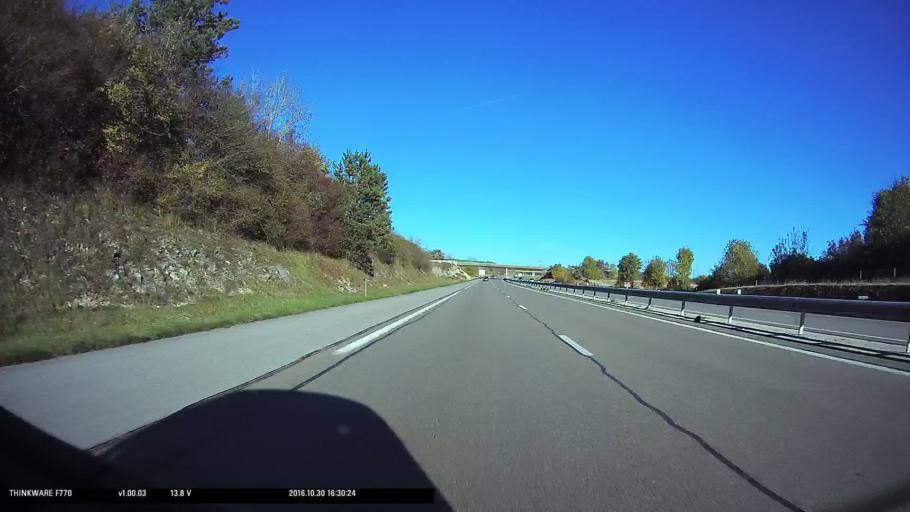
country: FR
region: Franche-Comte
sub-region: Departement du Doubs
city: Roulans
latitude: 47.3423
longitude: 6.2404
